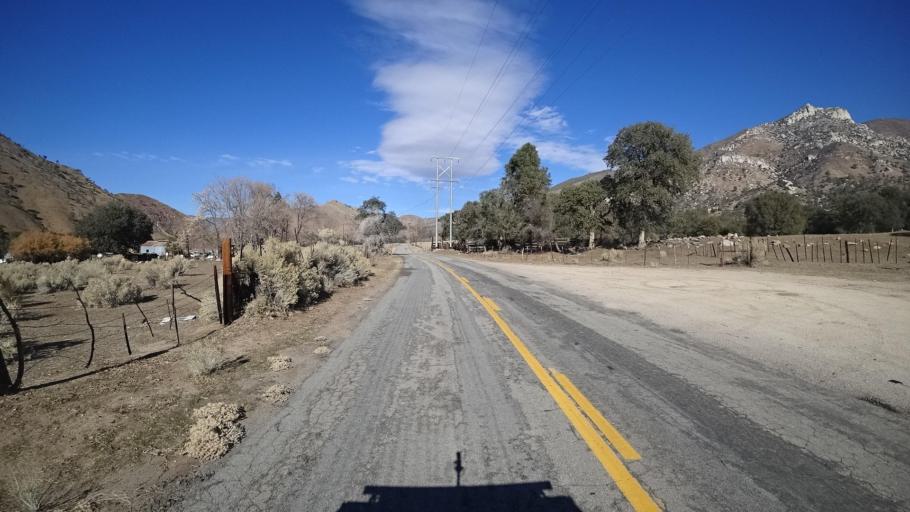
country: US
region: California
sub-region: Kern County
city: Bodfish
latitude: 35.5353
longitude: -118.5110
